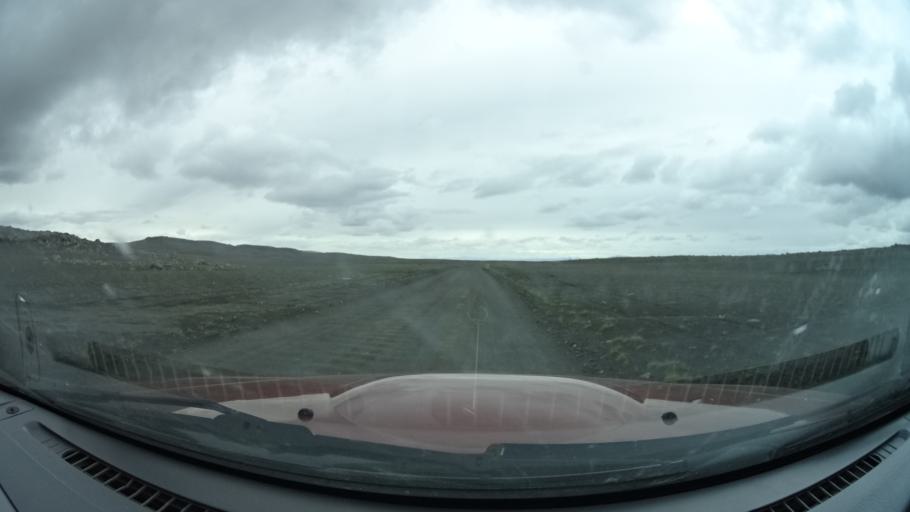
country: IS
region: Northeast
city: Husavik
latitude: 65.8009
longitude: -16.3508
